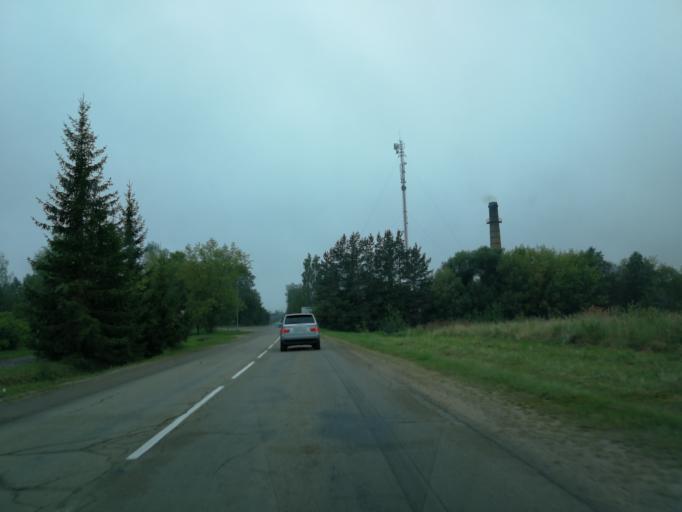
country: LV
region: Preilu Rajons
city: Preili
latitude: 56.3014
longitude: 26.7164
